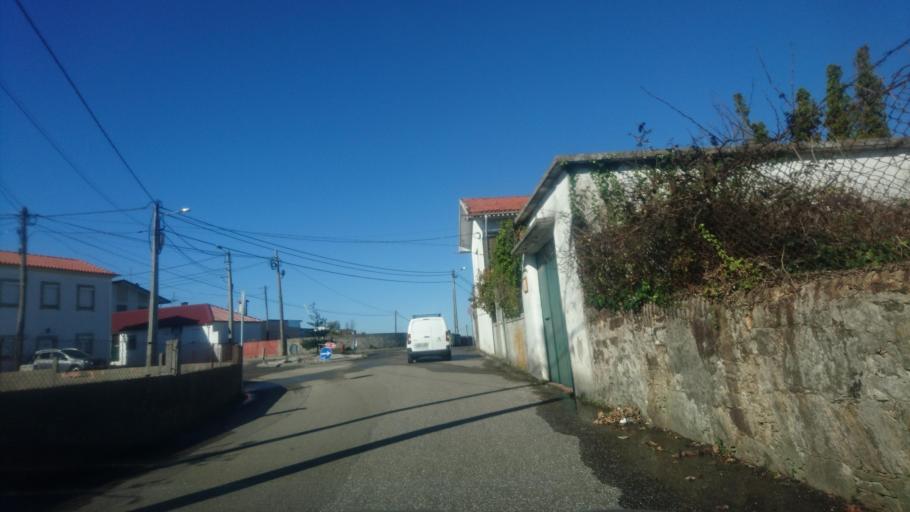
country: PT
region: Aveiro
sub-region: Oliveira de Azemeis
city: Sao Roque
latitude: 40.8842
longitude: -8.4578
